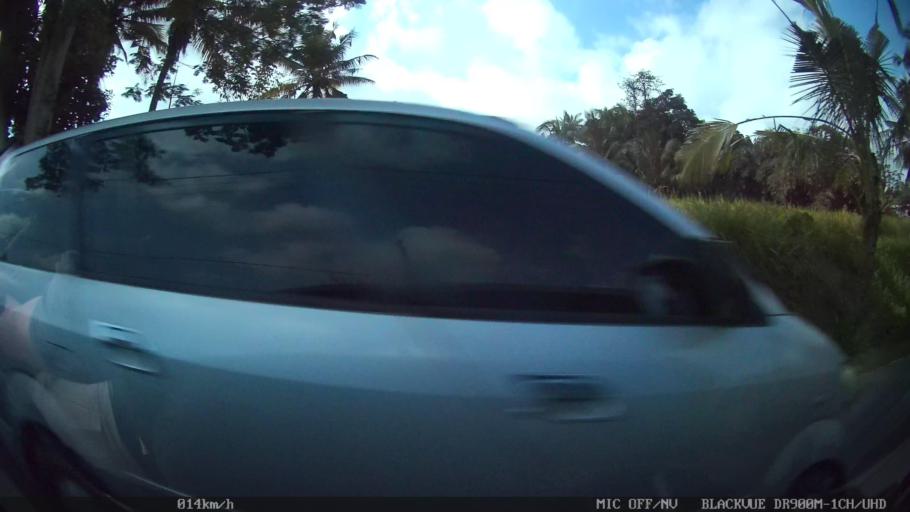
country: ID
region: Bali
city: Banjar Pesalakan
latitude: -8.4993
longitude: 115.2968
